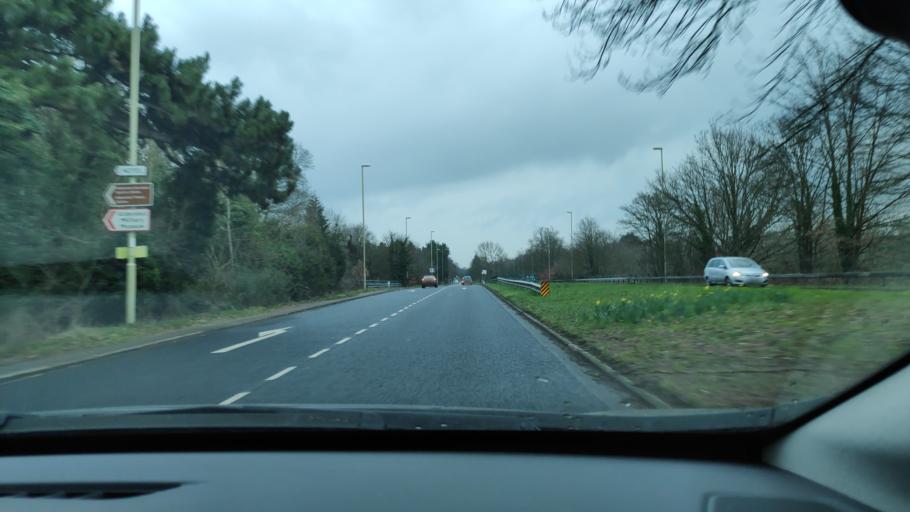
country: GB
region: England
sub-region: Hampshire
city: Aldershot
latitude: 51.2611
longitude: -0.7675
